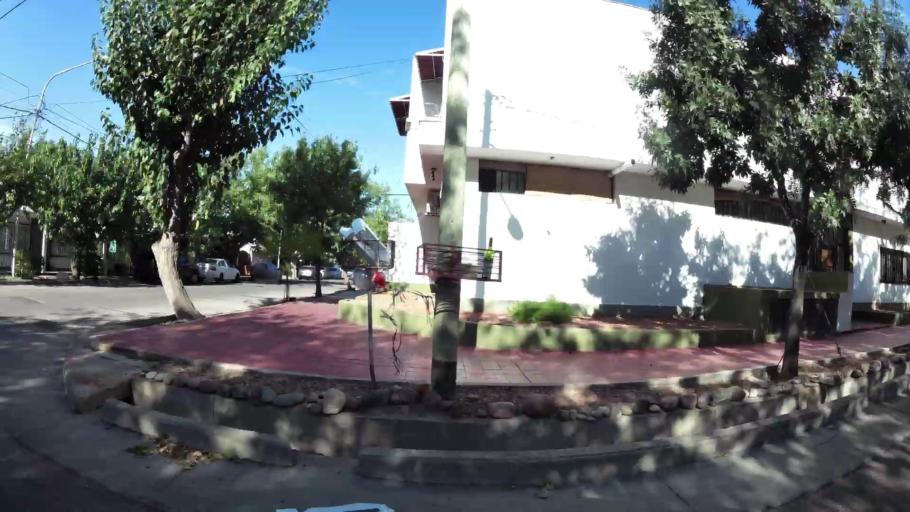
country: AR
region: Mendoza
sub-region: Departamento de Godoy Cruz
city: Godoy Cruz
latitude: -32.9131
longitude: -68.8247
